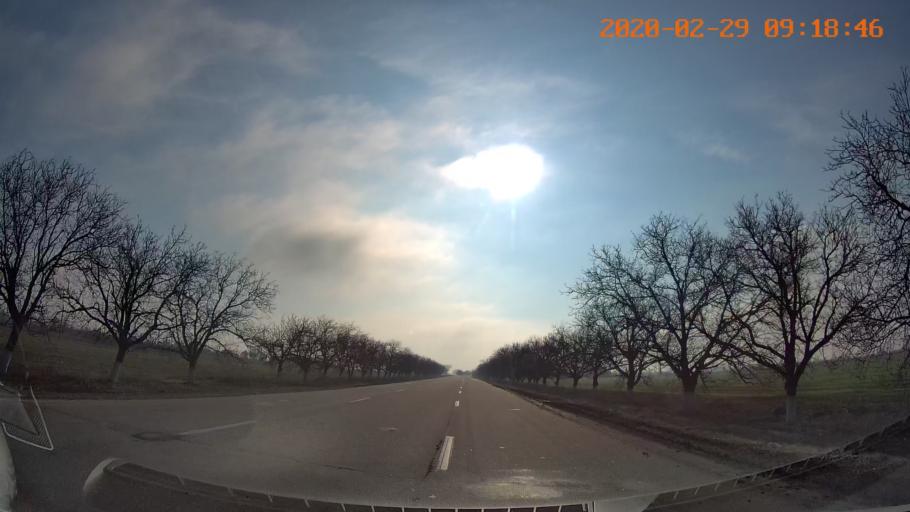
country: MD
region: Telenesti
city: Pervomaisc
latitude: 46.7704
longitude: 29.9291
